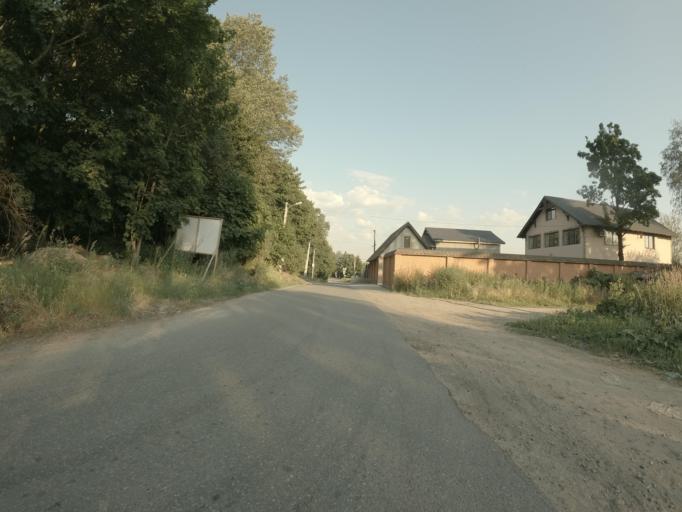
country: RU
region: Leningrad
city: Koltushi
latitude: 59.8875
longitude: 30.7121
